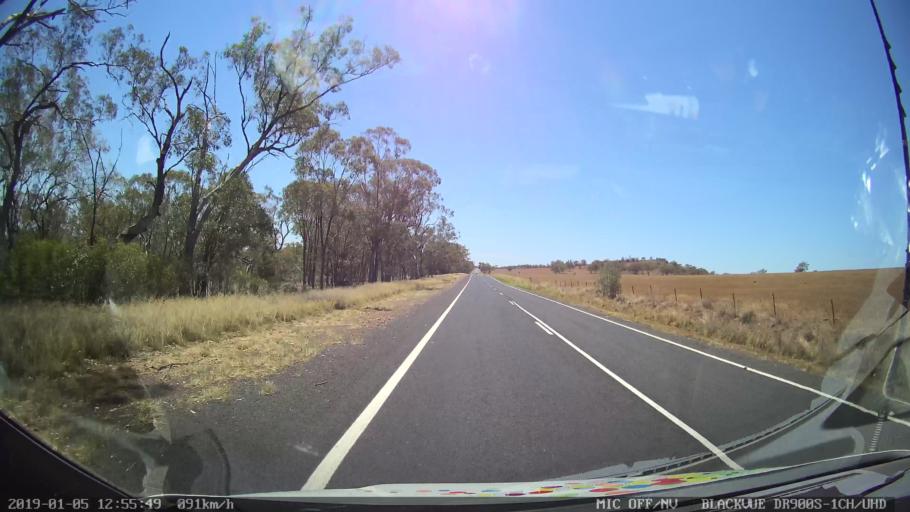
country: AU
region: New South Wales
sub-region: Warrumbungle Shire
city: Coonabarabran
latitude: -31.1190
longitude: 149.7116
